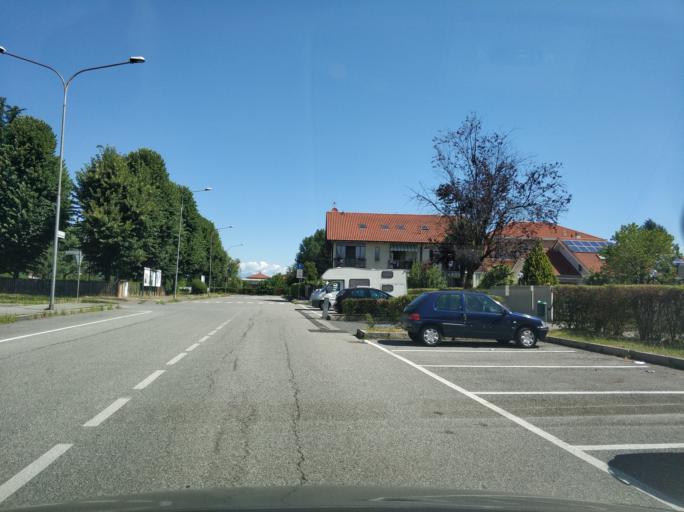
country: IT
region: Piedmont
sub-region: Provincia di Torino
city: Settimo Torinese
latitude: 45.1435
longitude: 7.7606
